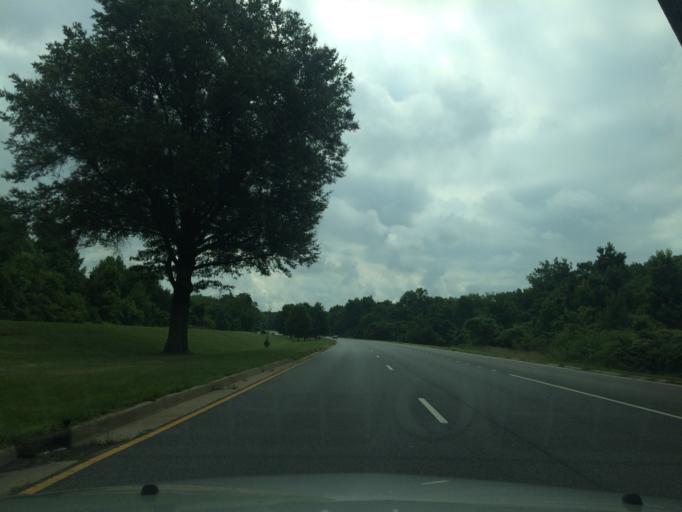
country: US
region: Maryland
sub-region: Prince George's County
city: Suitland
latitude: 38.8354
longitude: -76.9200
